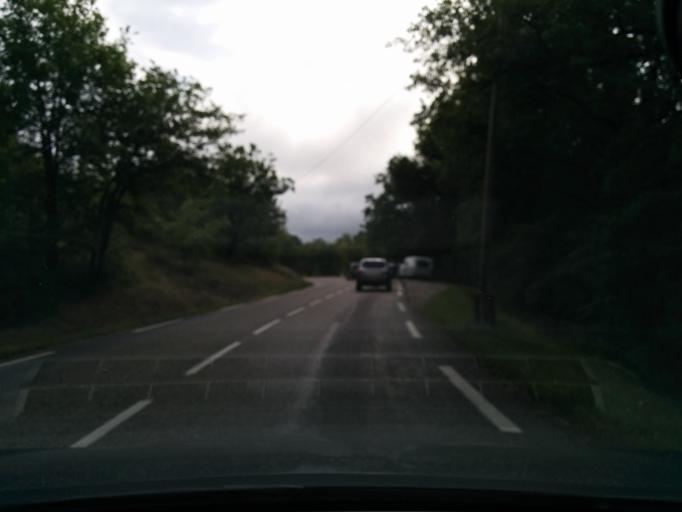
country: FR
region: Midi-Pyrenees
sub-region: Departement du Lot
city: Luzech
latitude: 44.3891
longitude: 1.3374
